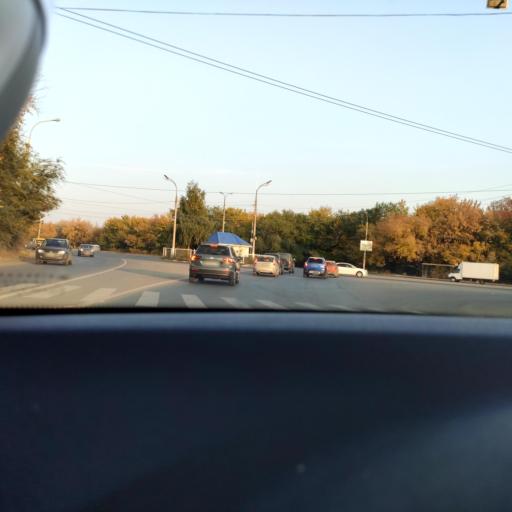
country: RU
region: Samara
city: Smyshlyayevka
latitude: 53.2513
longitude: 50.3586
